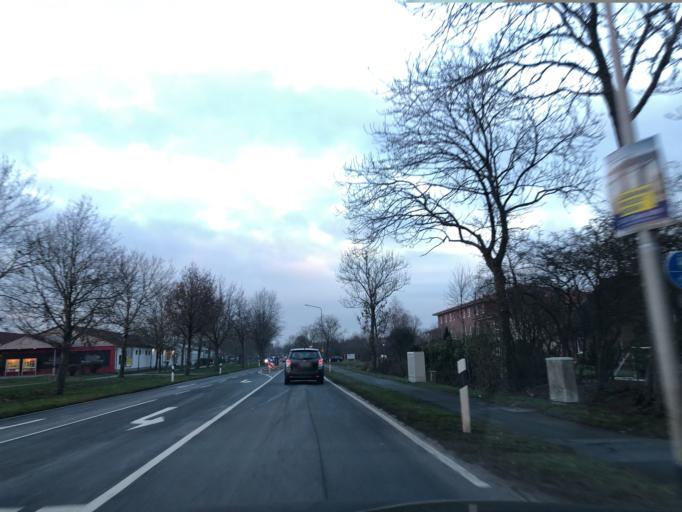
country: DE
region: Lower Saxony
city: Lemwerder
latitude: 53.1536
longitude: 8.6088
